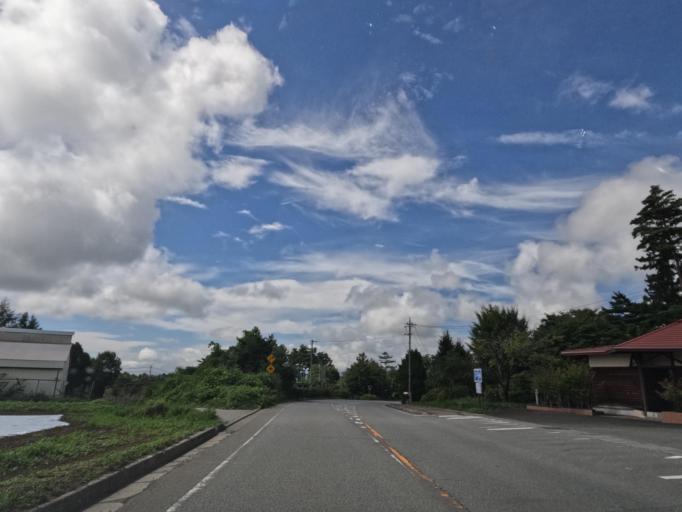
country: JP
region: Yamanashi
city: Nirasaki
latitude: 35.8888
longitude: 138.4195
